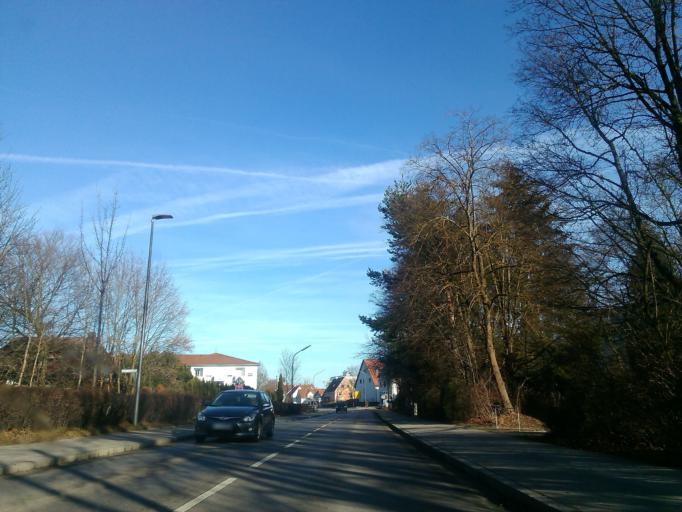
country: DE
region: Bavaria
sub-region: Swabia
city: Aichach
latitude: 48.4658
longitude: 11.1240
